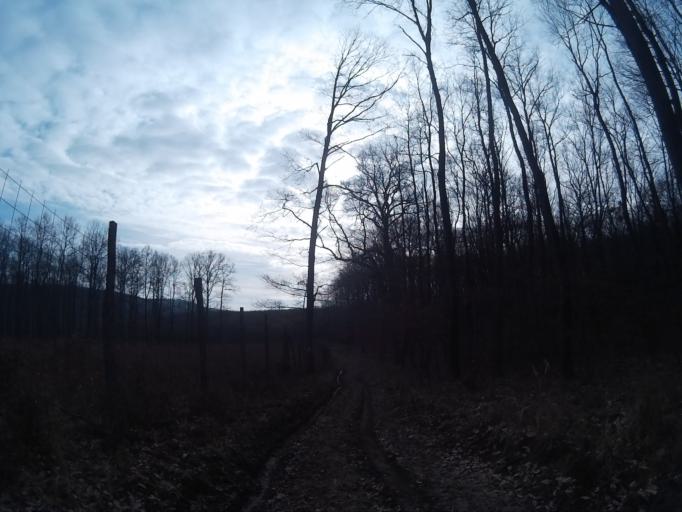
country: HU
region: Komarom-Esztergom
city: Tarjan
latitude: 47.5980
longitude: 18.4695
